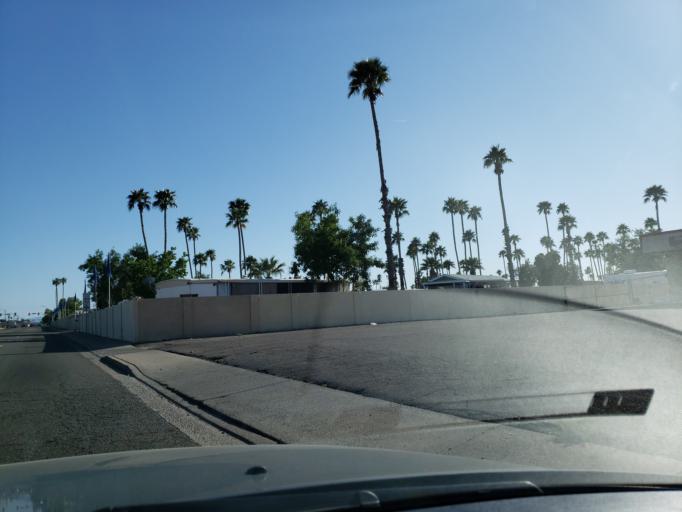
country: US
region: Arizona
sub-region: Maricopa County
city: Glendale
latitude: 33.5447
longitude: -112.1687
